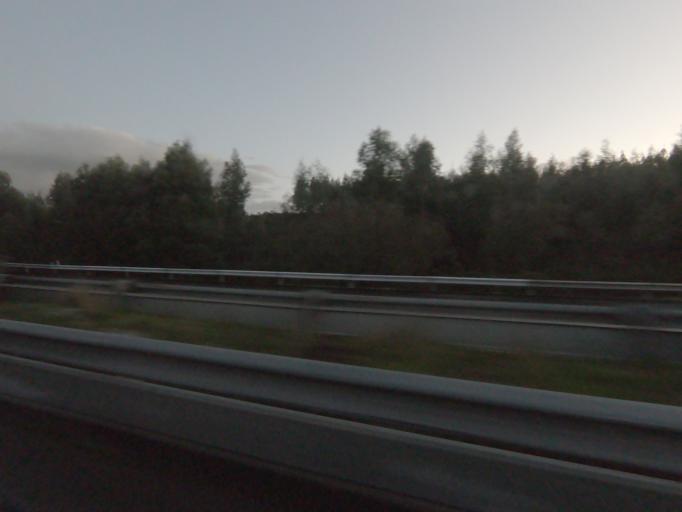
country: PT
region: Porto
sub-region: Paredes
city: Recarei
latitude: 41.1752
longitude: -8.4184
